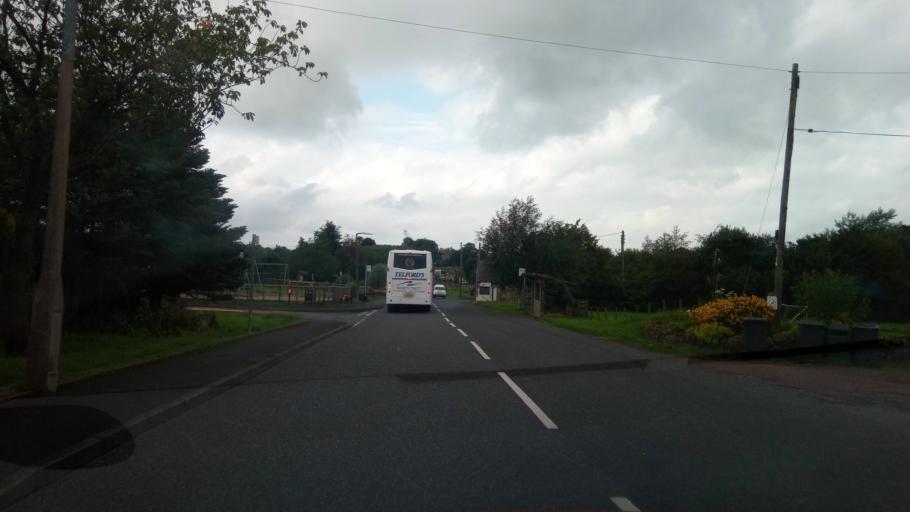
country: GB
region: Scotland
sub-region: Dumfries and Galloway
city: Langholm
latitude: 55.0869
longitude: -2.9260
